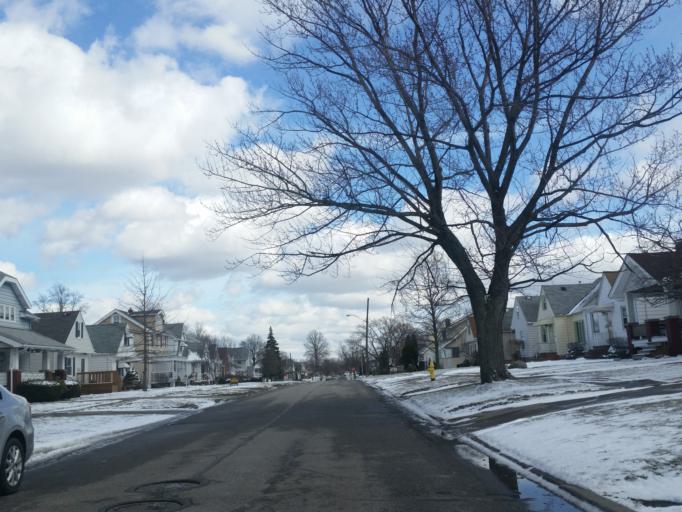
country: US
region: Ohio
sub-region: Cuyahoga County
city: Parma
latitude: 41.4149
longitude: -81.7088
